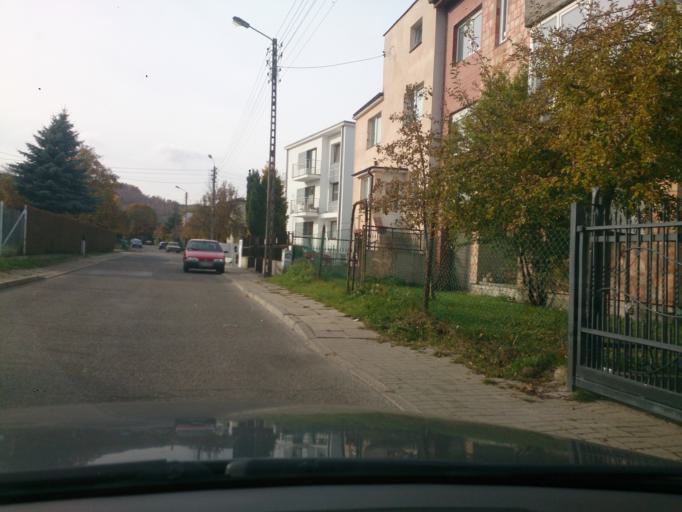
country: PL
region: Pomeranian Voivodeship
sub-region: Gdynia
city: Wielki Kack
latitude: 54.4860
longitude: 18.5182
